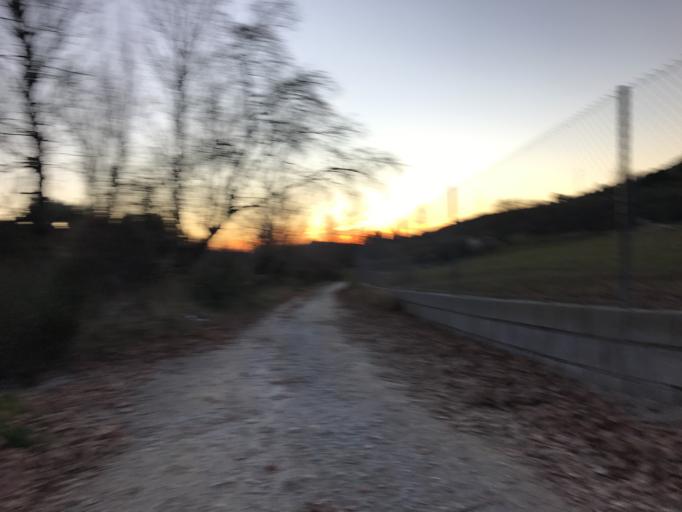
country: ES
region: Andalusia
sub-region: Provincia de Granada
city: Beas de Granada
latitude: 37.2264
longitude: -3.4762
